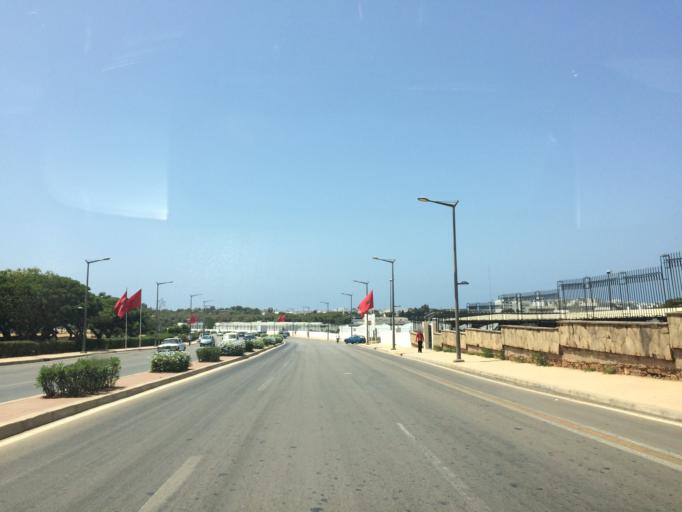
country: MA
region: Rabat-Sale-Zemmour-Zaer
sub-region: Rabat
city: Rabat
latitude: 33.9910
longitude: -6.8582
